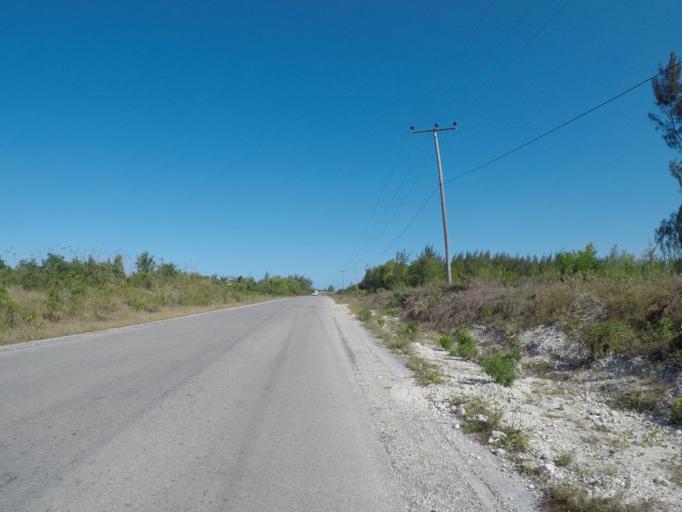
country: TZ
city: Kiwengwa
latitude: -6.1619
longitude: 39.5210
